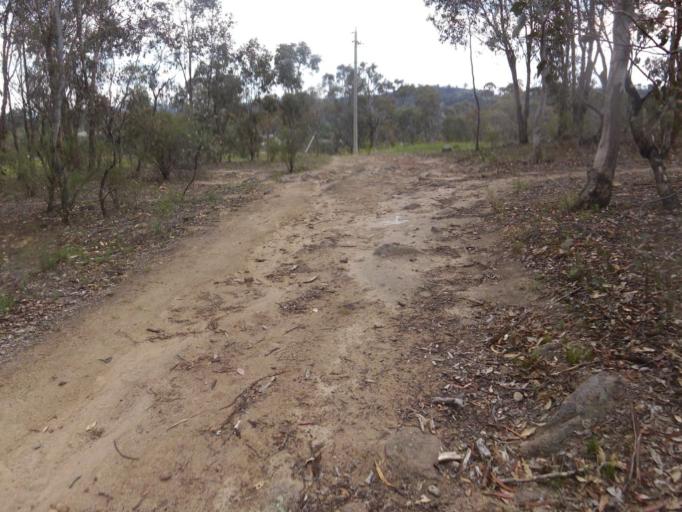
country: AU
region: Australian Capital Territory
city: Forrest
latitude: -35.3555
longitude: 149.1139
